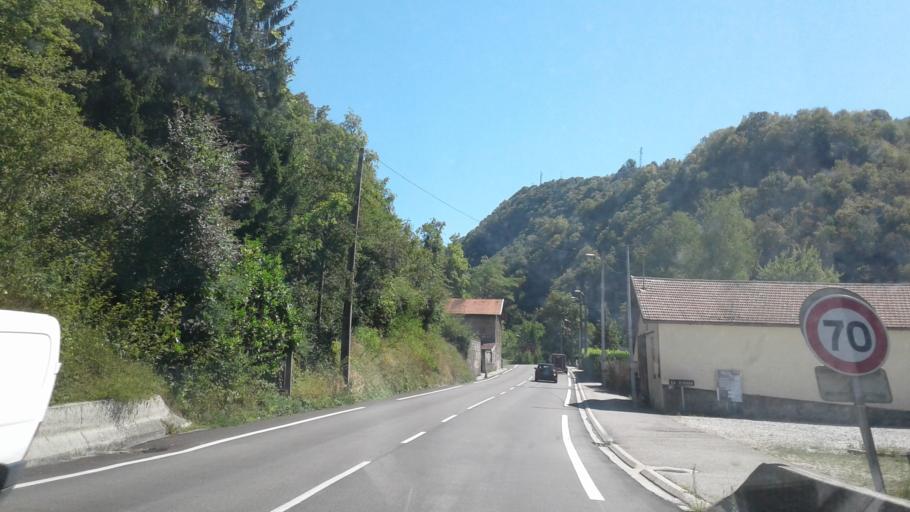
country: FR
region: Rhone-Alpes
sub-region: Departement de l'Ain
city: Tenay
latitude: 45.9298
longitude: 5.4942
